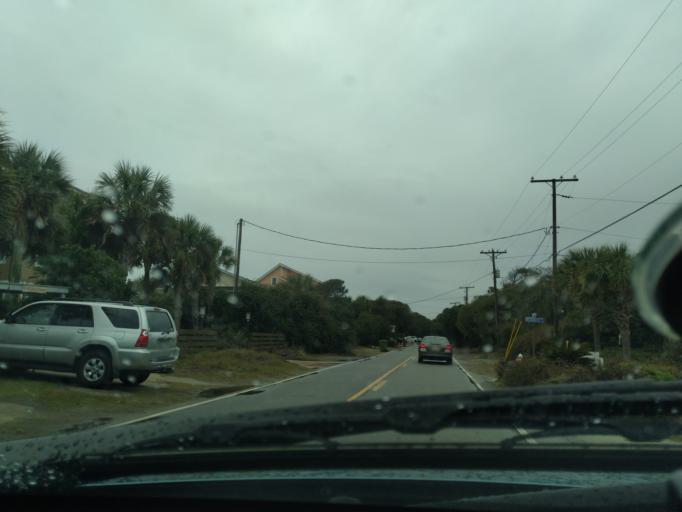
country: US
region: South Carolina
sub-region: Charleston County
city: Folly Beach
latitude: 32.6677
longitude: -79.9117
